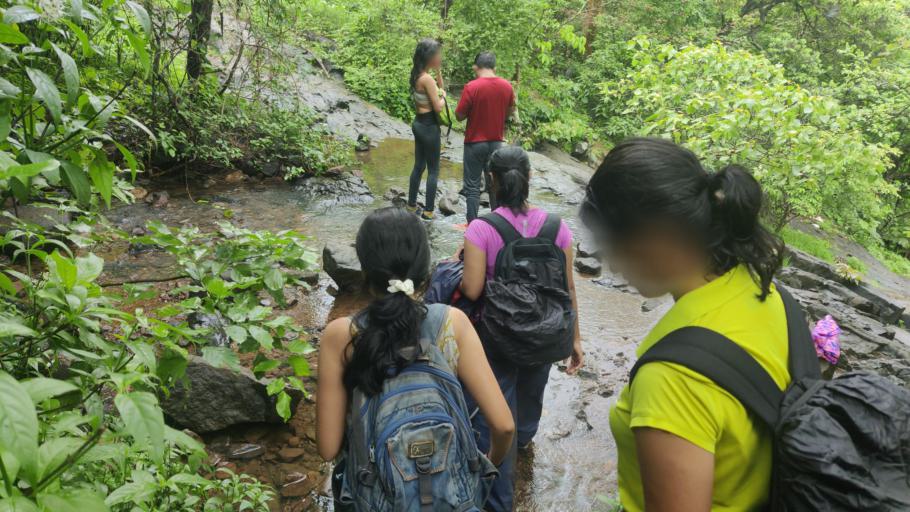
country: IN
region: Maharashtra
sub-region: Thane
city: Thane
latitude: 19.2401
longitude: 72.9574
